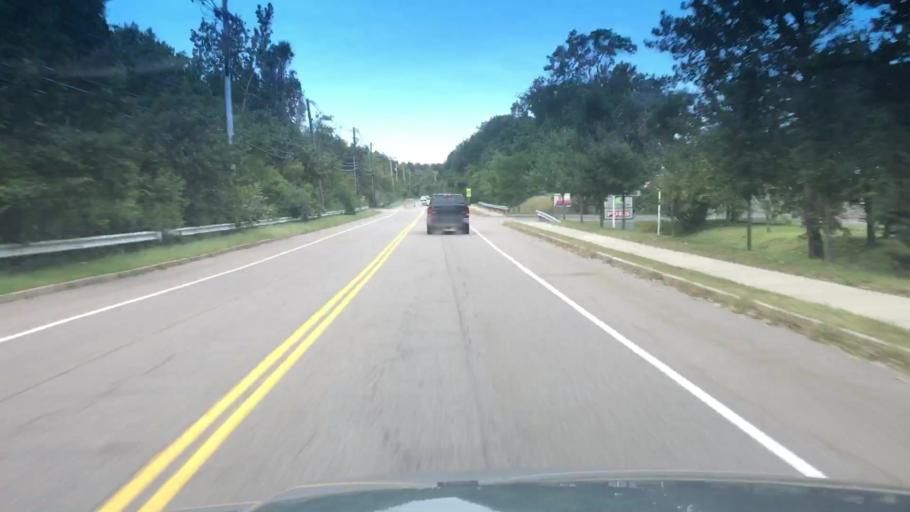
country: US
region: Massachusetts
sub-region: Norfolk County
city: Norwood
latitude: 42.1999
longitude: -71.1693
